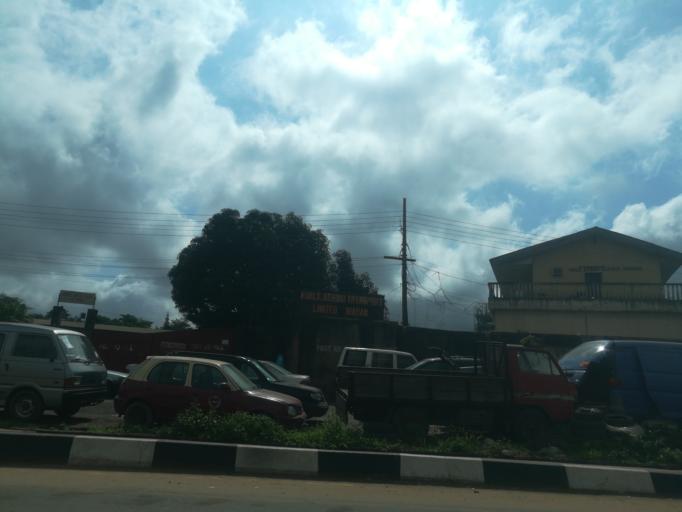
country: NG
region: Oyo
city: Ibadan
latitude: 7.3329
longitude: 3.8690
